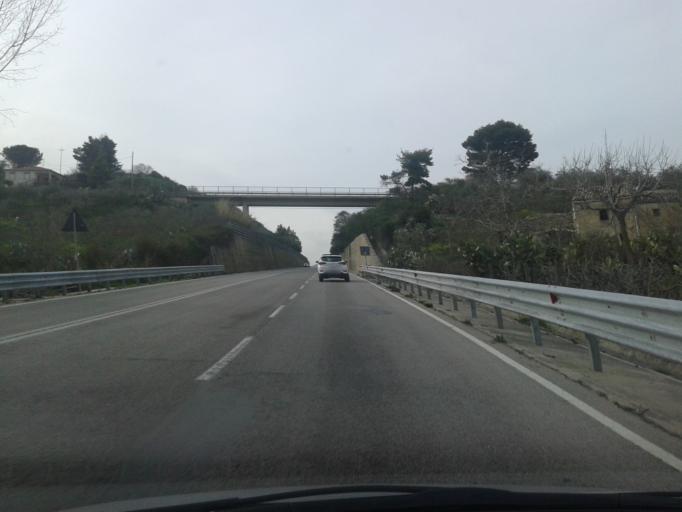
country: IT
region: Sicily
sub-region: Palermo
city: Giacalone
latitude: 38.0316
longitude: 13.2577
